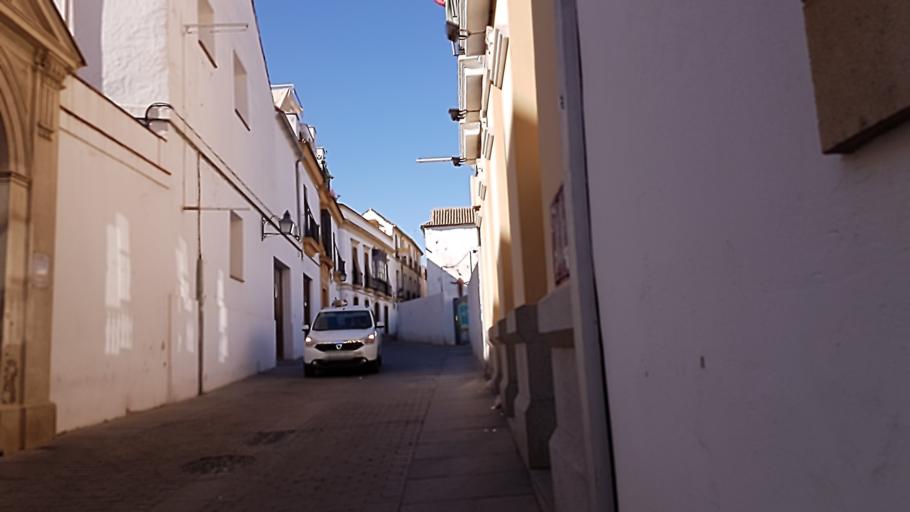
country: ES
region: Andalusia
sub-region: Province of Cordoba
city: Cordoba
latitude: 37.8826
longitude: -4.7772
